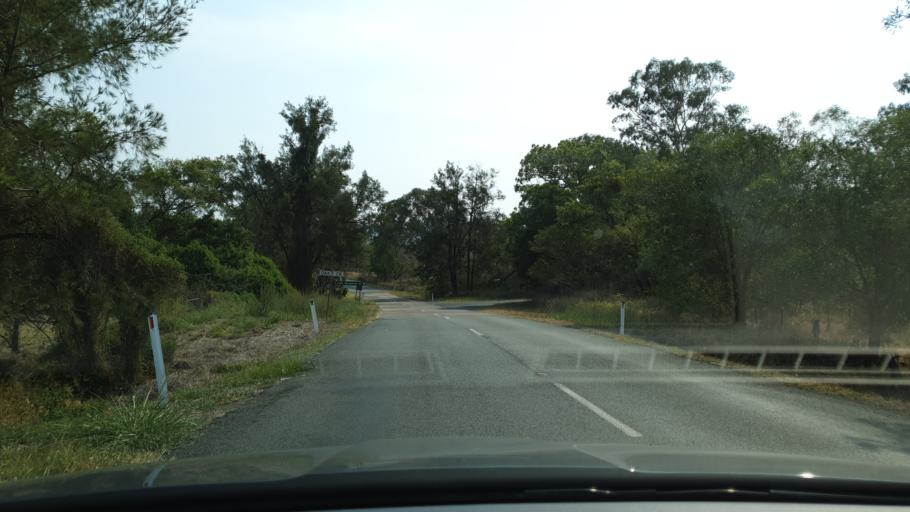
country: AU
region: Queensland
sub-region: Ipswich
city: Deebing Heights
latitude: -28.1445
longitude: 152.5665
